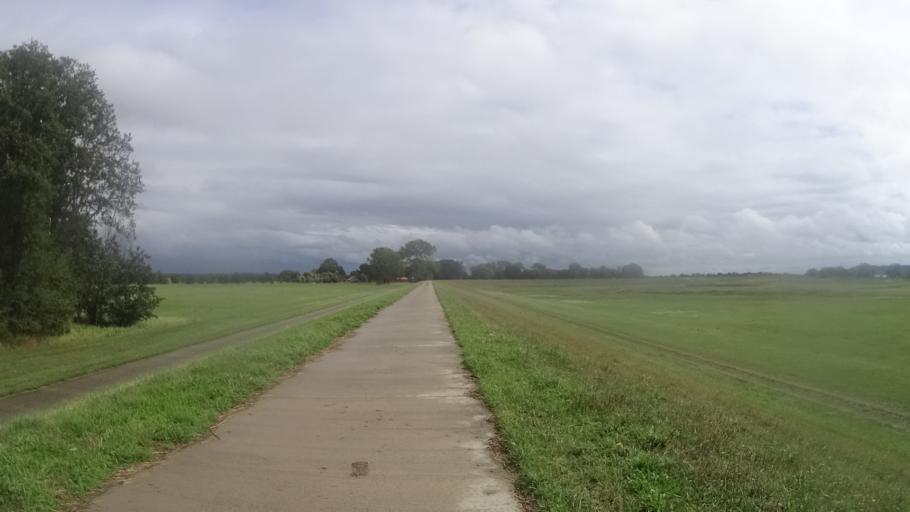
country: DE
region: Lower Saxony
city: Neu Darchau
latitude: 53.2356
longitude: 10.9073
